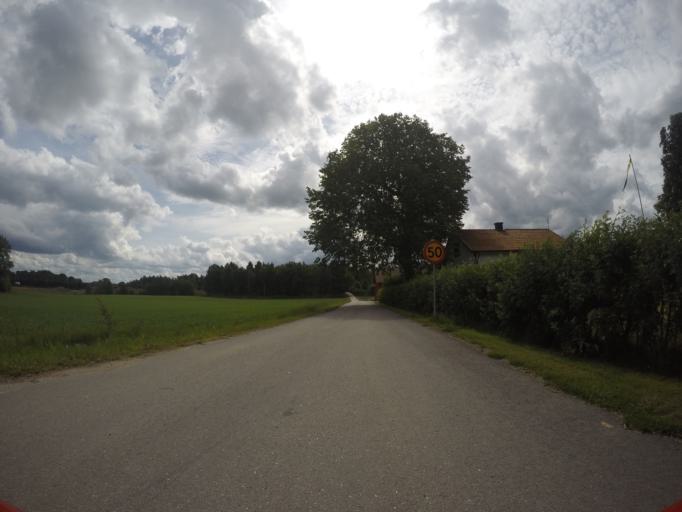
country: SE
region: Vaestra Goetaland
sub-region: Trollhattan
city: Trollhattan
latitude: 58.2337
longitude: 12.3133
